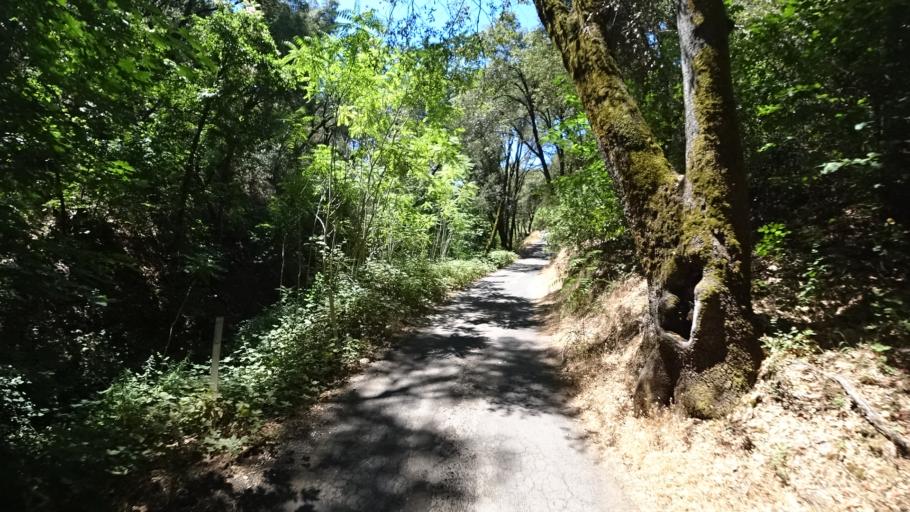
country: US
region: California
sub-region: Calaveras County
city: Forest Meadows
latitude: 38.1427
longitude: -120.4172
